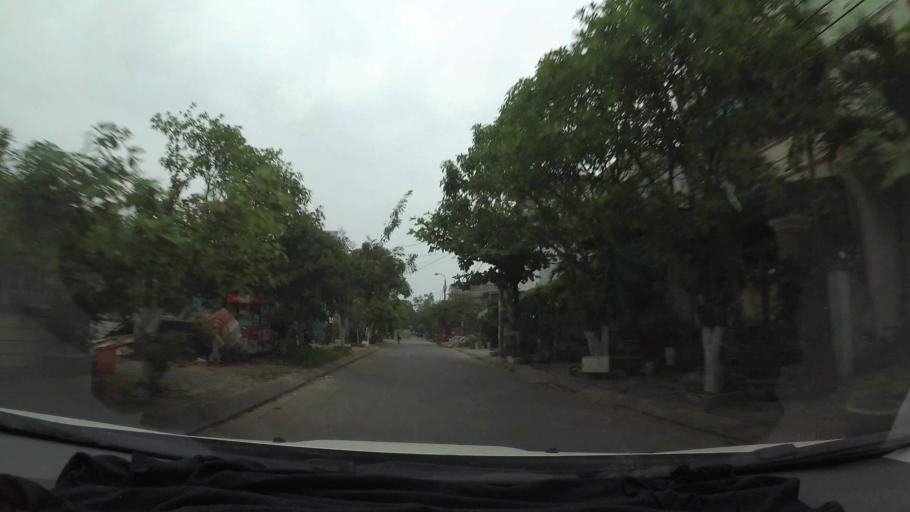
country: VN
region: Da Nang
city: Thanh Khe
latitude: 16.0510
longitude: 108.1770
